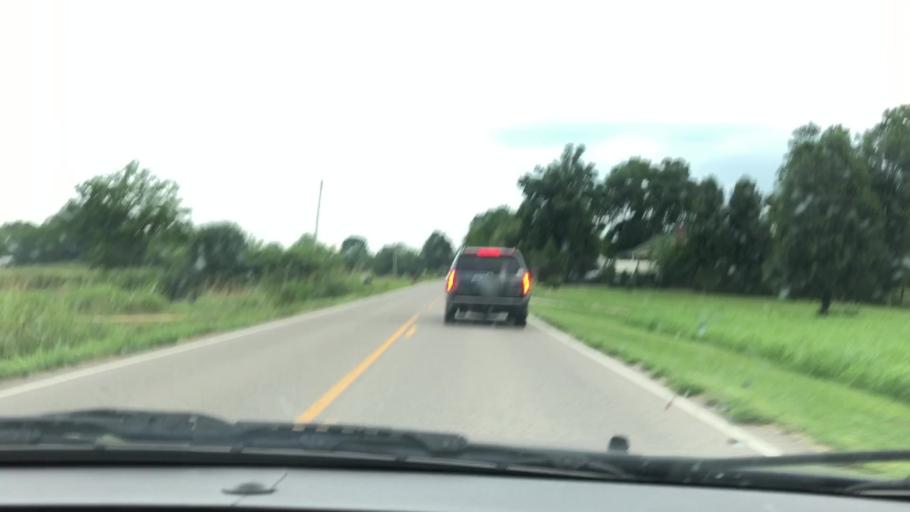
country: US
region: Tennessee
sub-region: Maury County
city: Spring Hill
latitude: 35.7287
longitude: -87.0115
